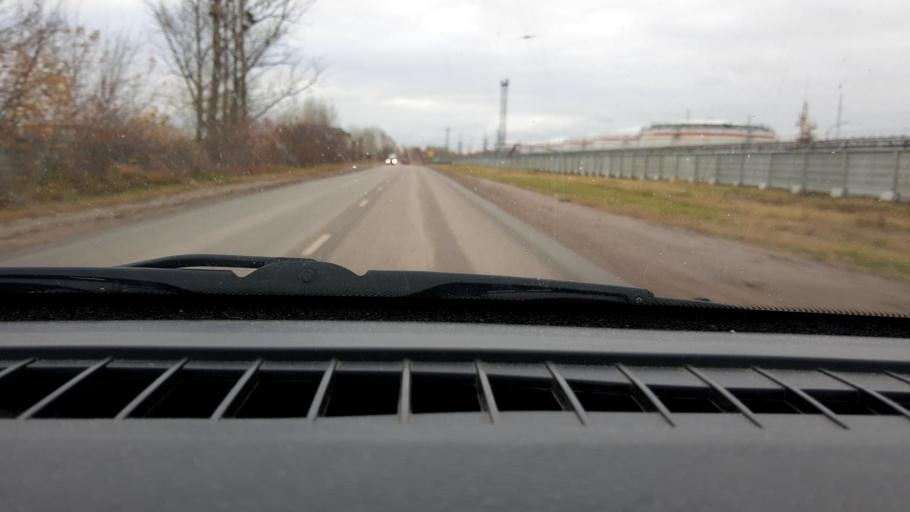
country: RU
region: Nizjnij Novgorod
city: Kstovo
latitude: 56.1205
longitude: 44.1403
